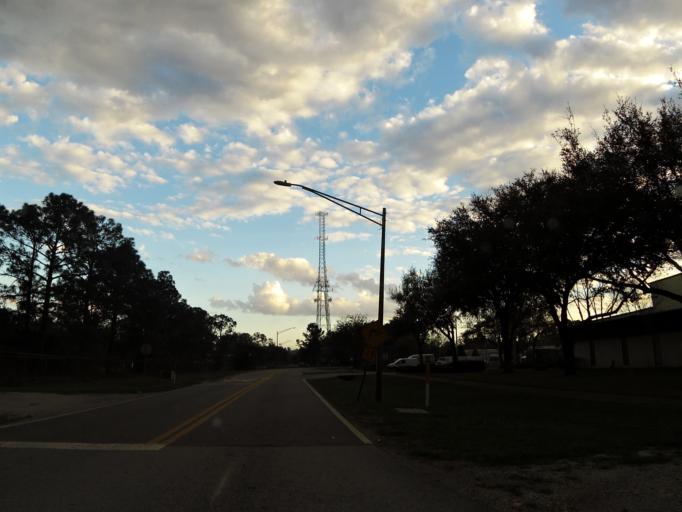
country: US
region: Florida
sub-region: Saint Johns County
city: Fruit Cove
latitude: 30.1882
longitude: -81.5677
